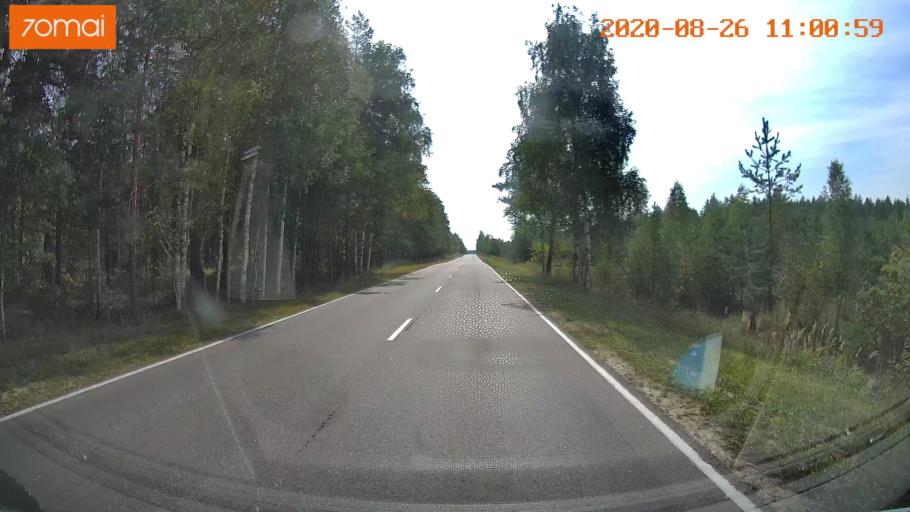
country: RU
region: Rjazan
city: Izhevskoye
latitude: 54.5685
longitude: 41.2192
